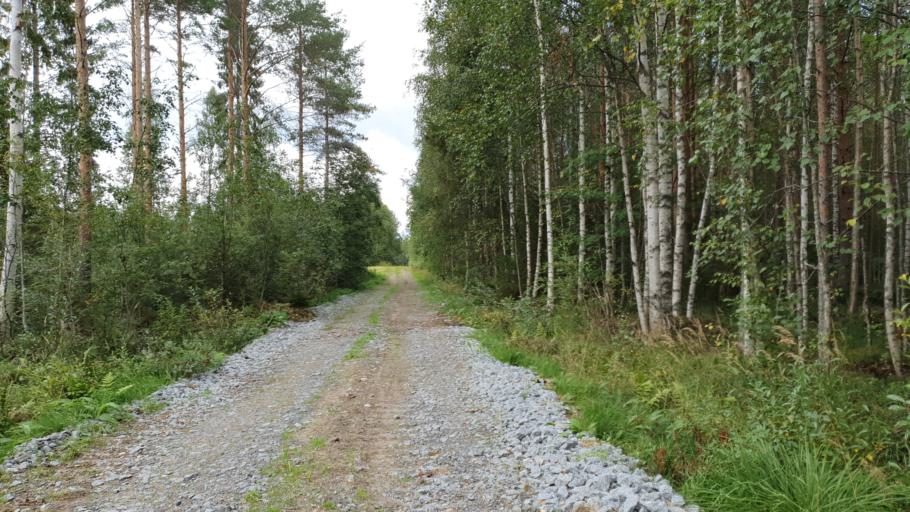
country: FI
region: Kainuu
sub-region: Kehys-Kainuu
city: Kuhmo
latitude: 64.1328
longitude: 29.4502
